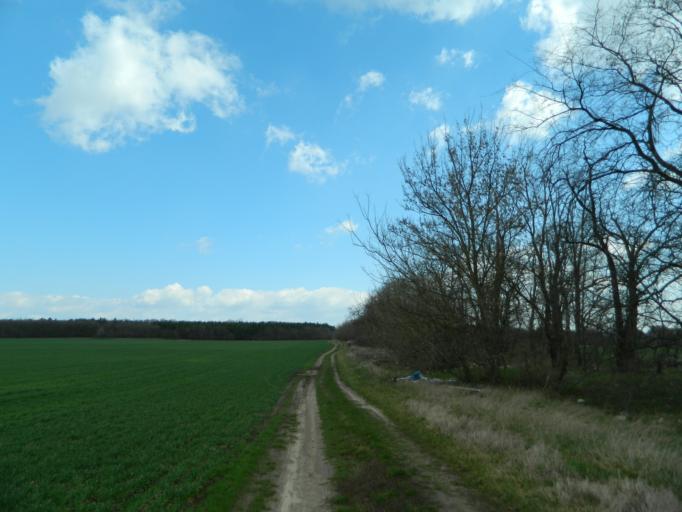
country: HU
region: Fejer
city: Szabadbattyan
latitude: 47.1408
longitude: 18.3734
